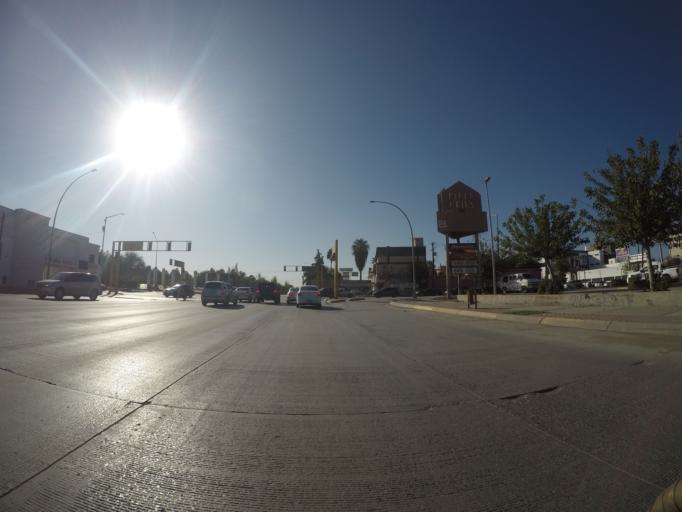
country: MX
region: Chihuahua
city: Ciudad Juarez
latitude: 31.7377
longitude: -106.4583
